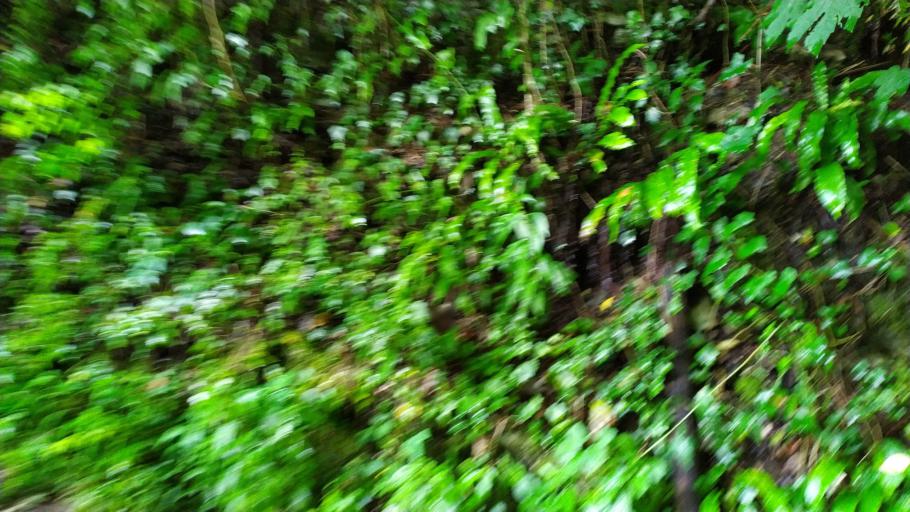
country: IT
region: Veneto
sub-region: Provincia di Vicenza
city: Torrebelvicino
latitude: 45.6952
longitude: 11.3283
